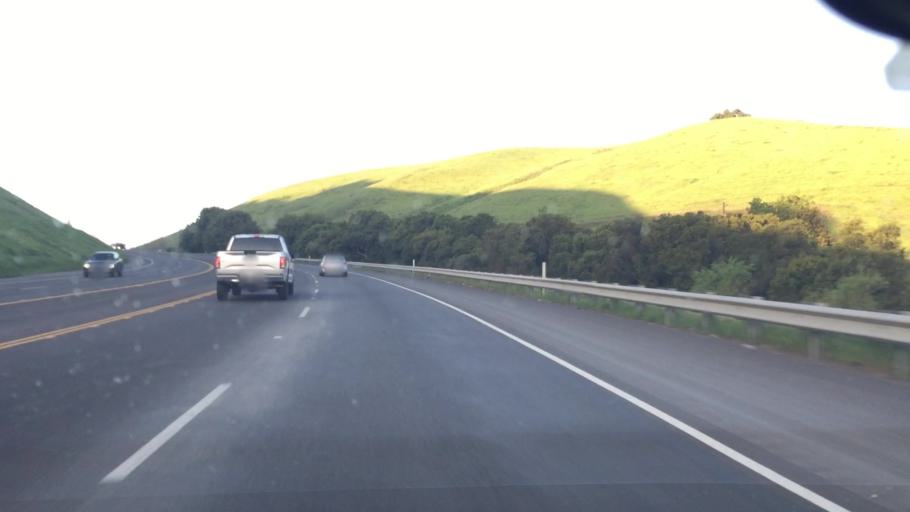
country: US
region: California
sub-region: Alameda County
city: Livermore
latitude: 37.6245
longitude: -121.8078
